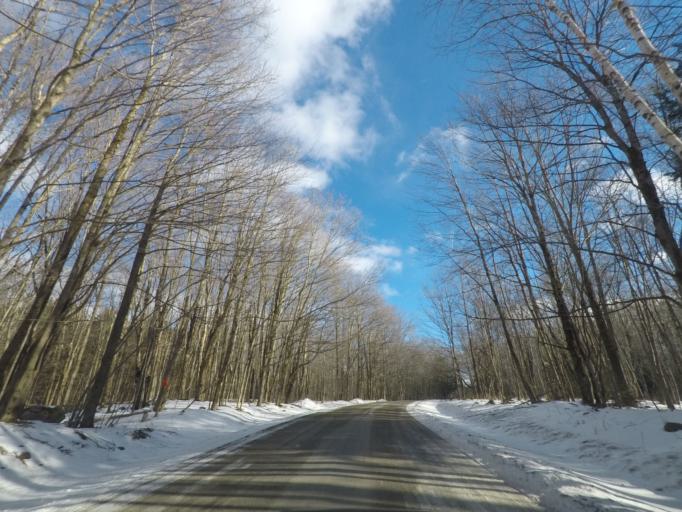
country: US
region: New York
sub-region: Rensselaer County
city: Poestenkill
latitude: 42.7478
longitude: -73.4817
